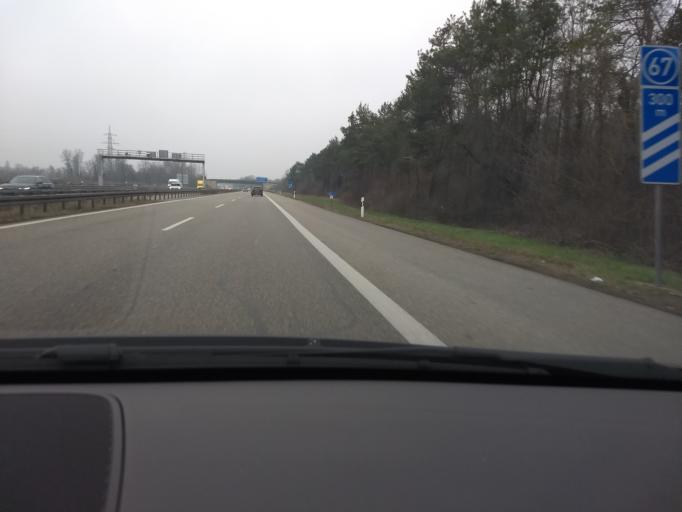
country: FR
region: Alsace
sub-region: Departement du Haut-Rhin
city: Kembs
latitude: 47.6740
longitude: 7.5238
